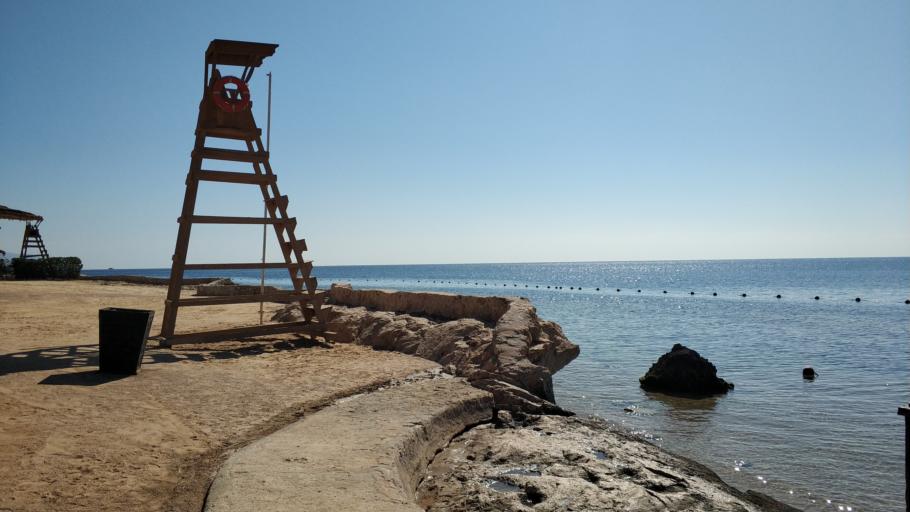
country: EG
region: South Sinai
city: Sharm el-Sheikh
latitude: 27.9147
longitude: 34.3623
